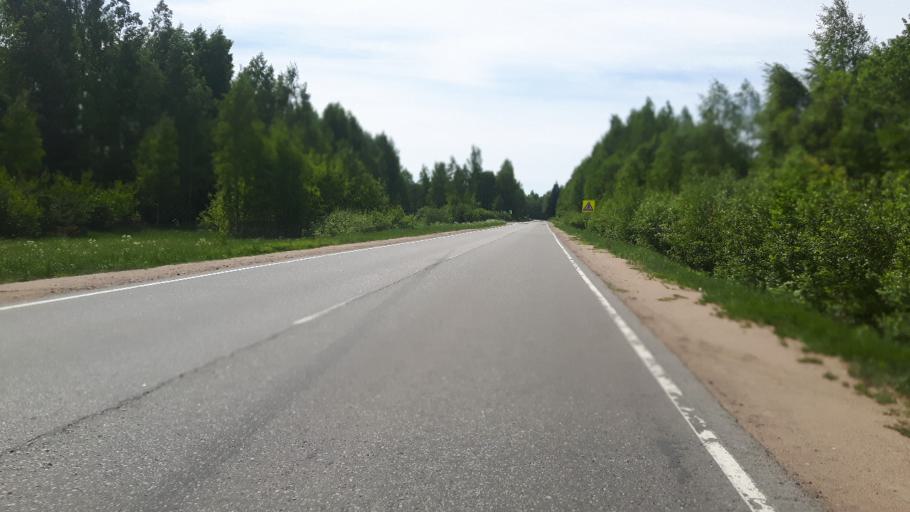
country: RU
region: Leningrad
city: Ust'-Luga
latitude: 59.6539
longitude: 28.2422
